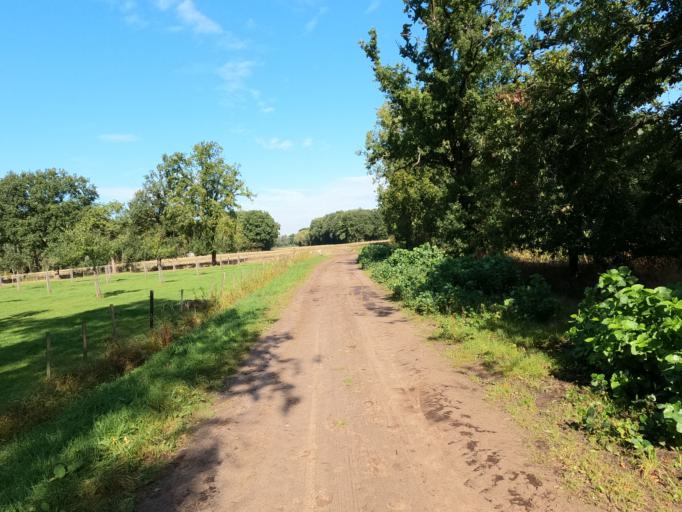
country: BE
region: Flanders
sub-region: Provincie Antwerpen
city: Lille
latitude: 51.2567
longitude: 4.8453
